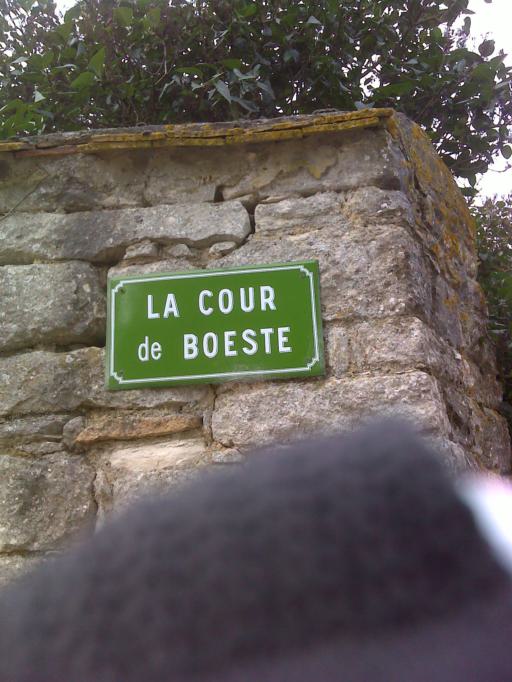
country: FR
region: Haute-Normandie
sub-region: Departement de l'Eure
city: Ivry-la-Bataille
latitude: 48.9082
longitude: 1.4852
